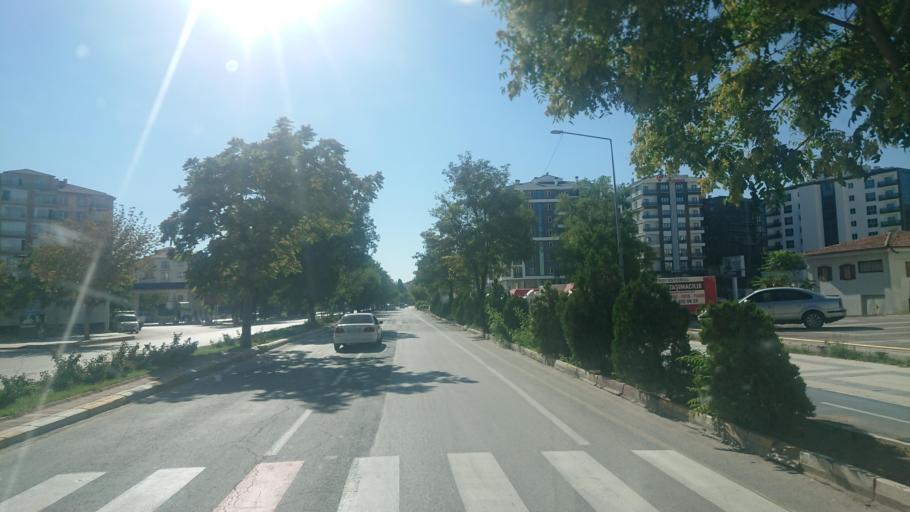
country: TR
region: Aksaray
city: Aksaray
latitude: 38.3642
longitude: 34.0143
